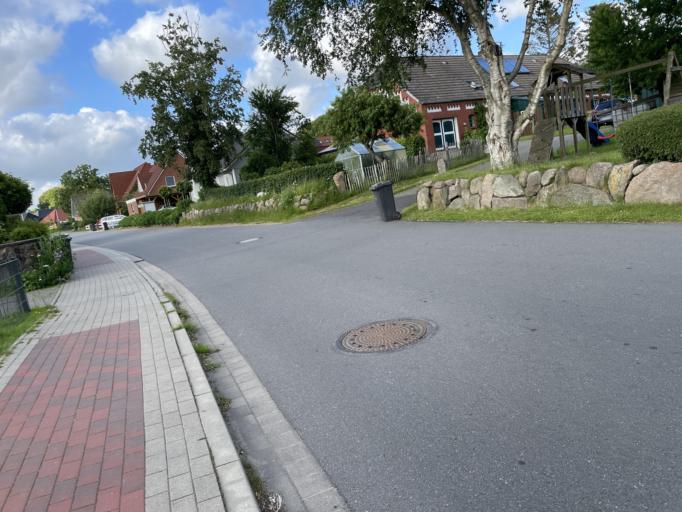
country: DE
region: Schleswig-Holstein
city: Mildstedt
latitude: 54.4593
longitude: 9.0942
